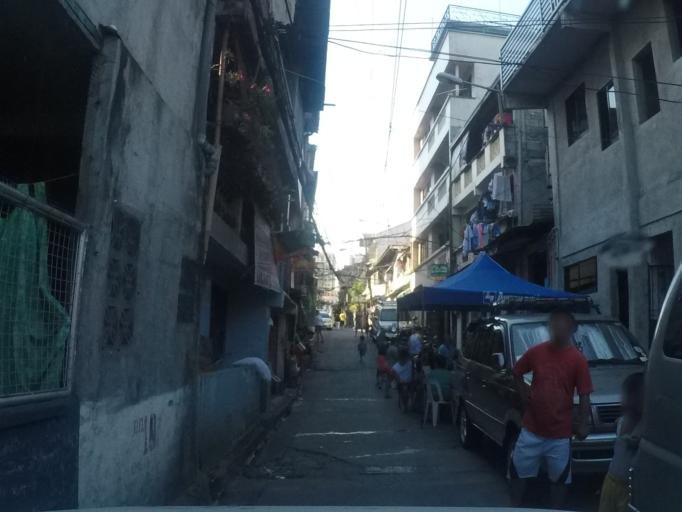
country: PH
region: Metro Manila
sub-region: San Juan
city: San Juan
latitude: 14.6050
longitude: 121.0501
